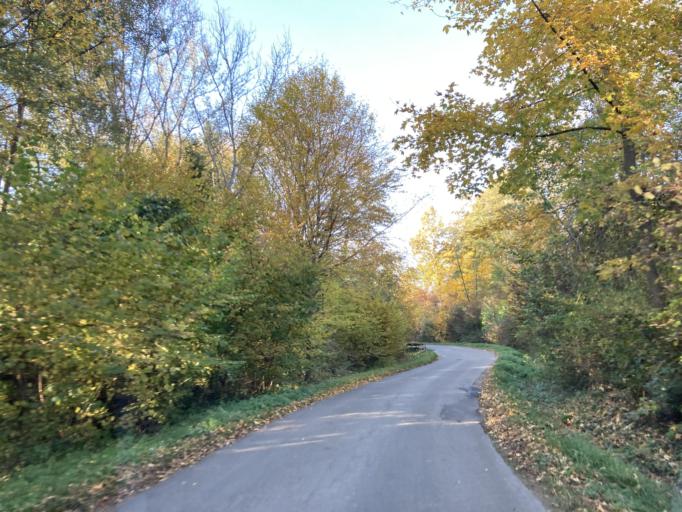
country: DE
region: Baden-Wuerttemberg
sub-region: Tuebingen Region
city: Mossingen
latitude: 48.3890
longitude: 9.0525
